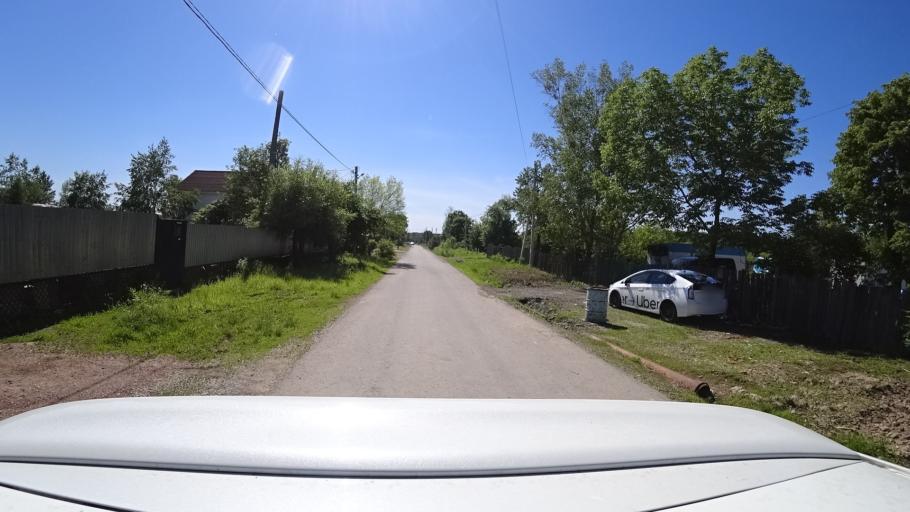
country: RU
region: Khabarovsk Krai
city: Topolevo
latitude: 48.5540
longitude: 135.1991
